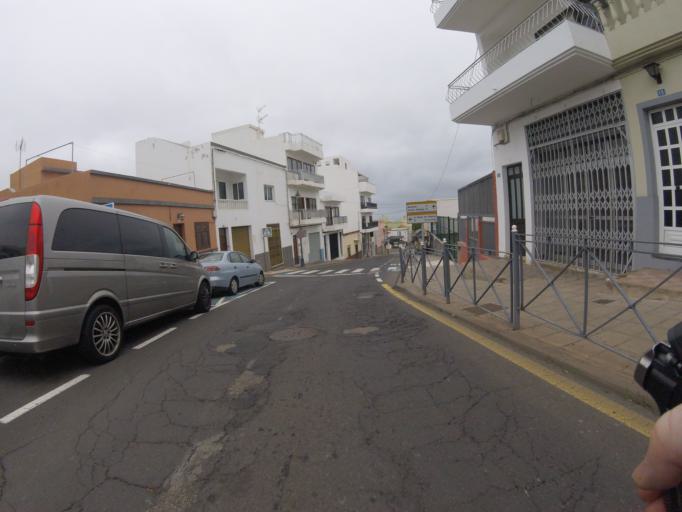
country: ES
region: Canary Islands
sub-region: Provincia de Santa Cruz de Tenerife
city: Tegueste
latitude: 28.5339
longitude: -16.3605
